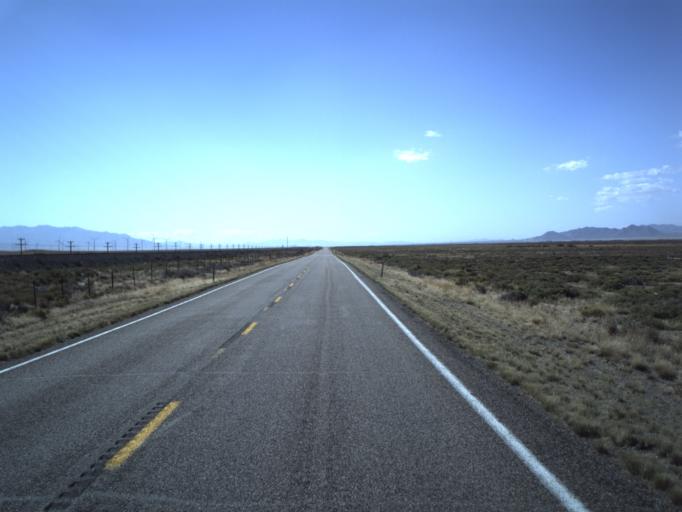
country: US
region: Utah
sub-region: Beaver County
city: Milford
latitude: 38.6440
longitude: -112.9830
